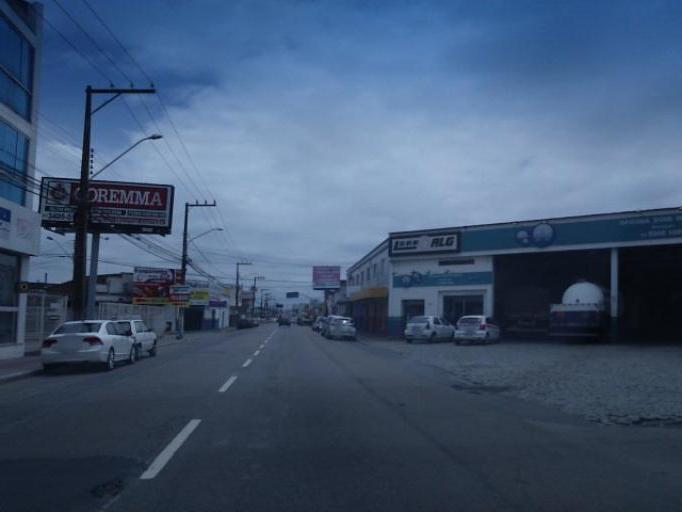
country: BR
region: Santa Catarina
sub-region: Itajai
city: Itajai
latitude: -26.8921
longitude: -48.6774
